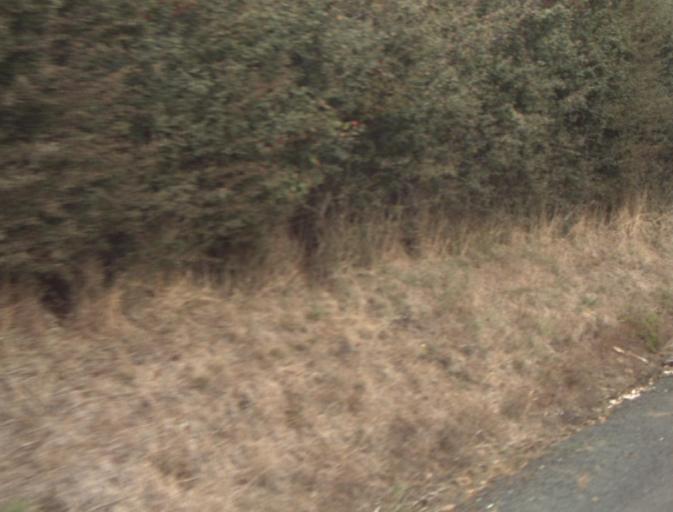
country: AU
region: Tasmania
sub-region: Northern Midlands
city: Evandale
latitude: -41.5279
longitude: 147.2451
